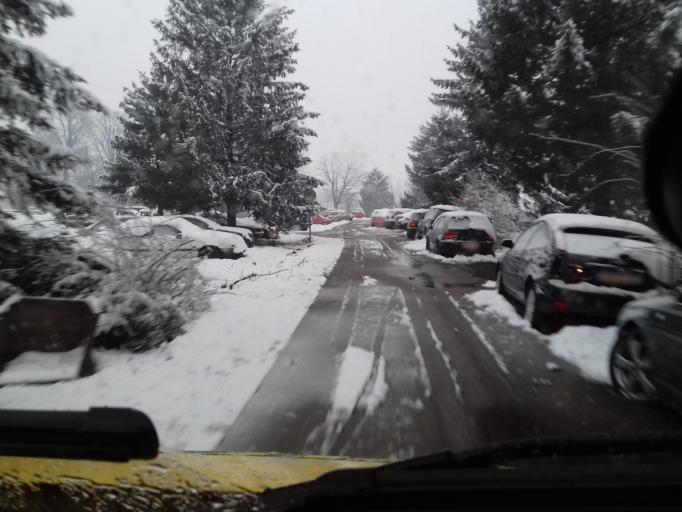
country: BA
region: Federation of Bosnia and Herzegovina
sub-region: Kanton Sarajevo
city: Sarajevo
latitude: 43.8130
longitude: 18.3284
